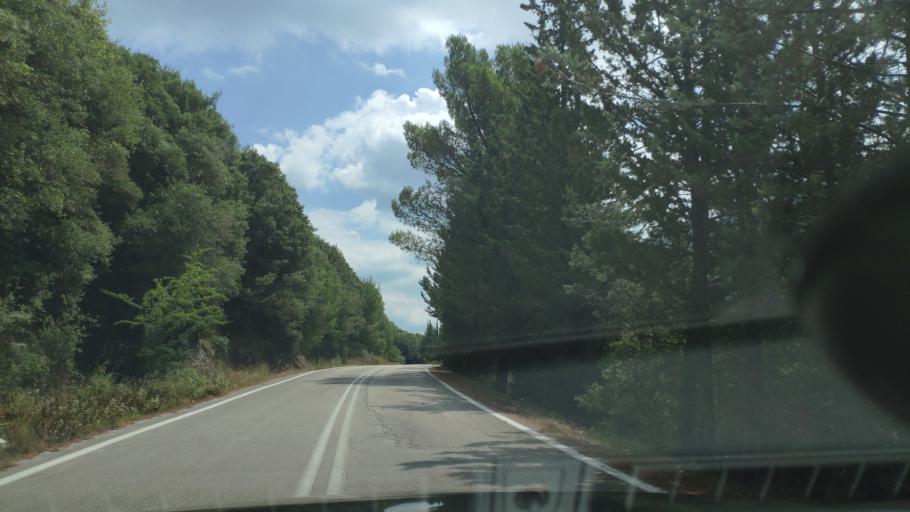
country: GR
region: Epirus
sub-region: Nomos Artas
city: Kampi
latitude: 39.2731
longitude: 20.9331
